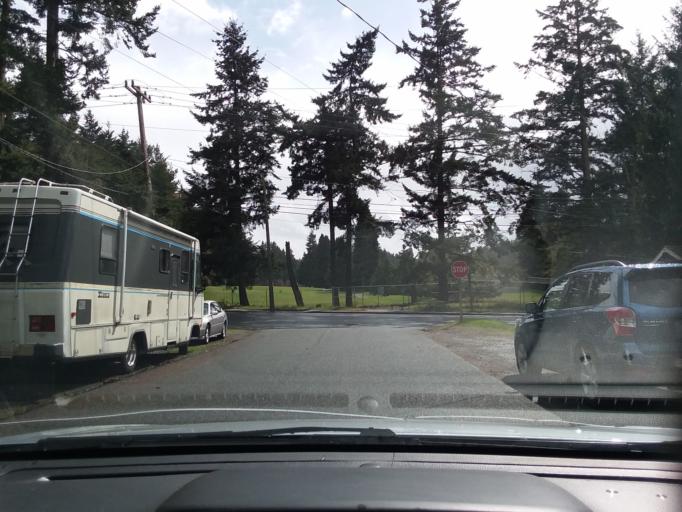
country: US
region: Washington
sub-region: King County
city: Shoreline
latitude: 47.7344
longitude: -122.3223
